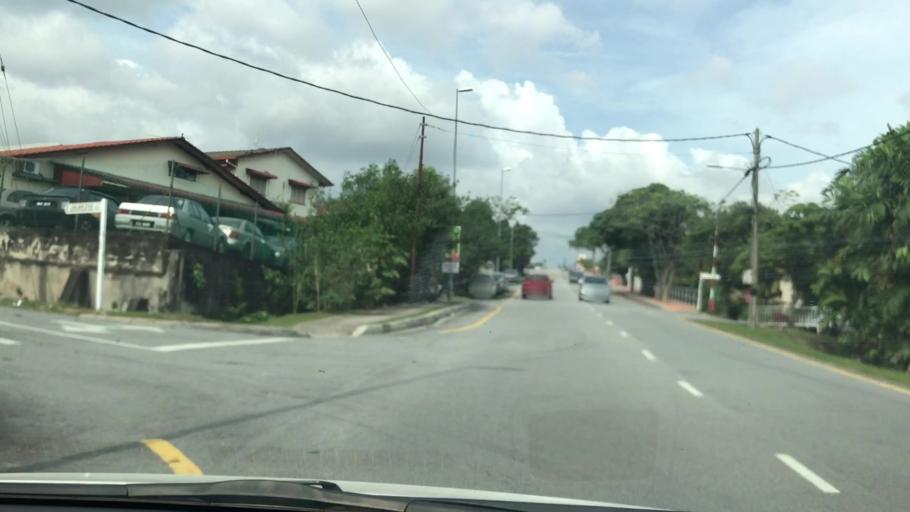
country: MY
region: Selangor
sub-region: Petaling
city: Petaling Jaya
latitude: 3.1118
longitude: 101.6254
